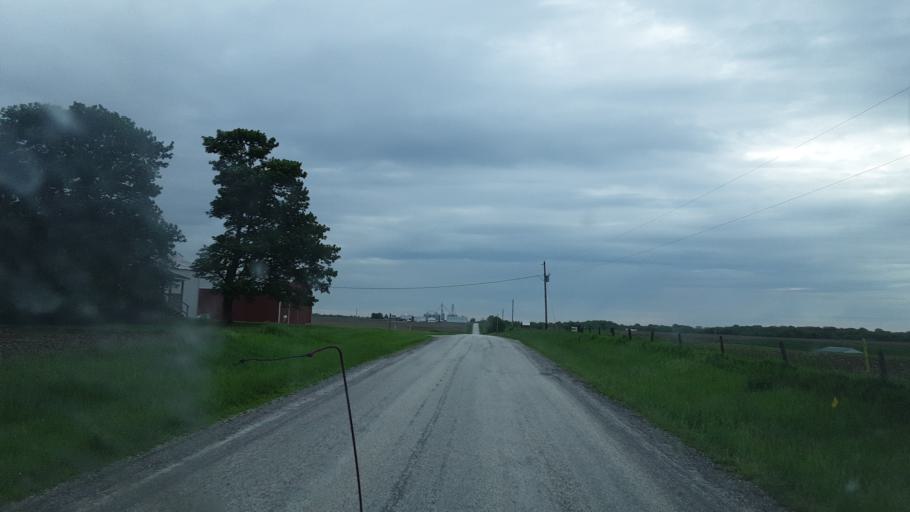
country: US
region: Illinois
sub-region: McDonough County
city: Macomb
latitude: 40.3817
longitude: -90.6328
